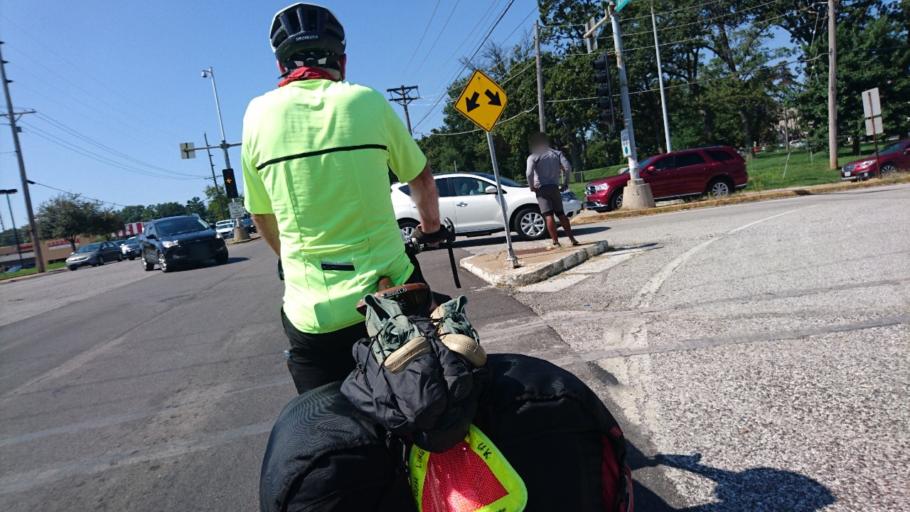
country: US
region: Missouri
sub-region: Saint Louis County
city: Warson Woods
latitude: 38.6009
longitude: -90.3967
